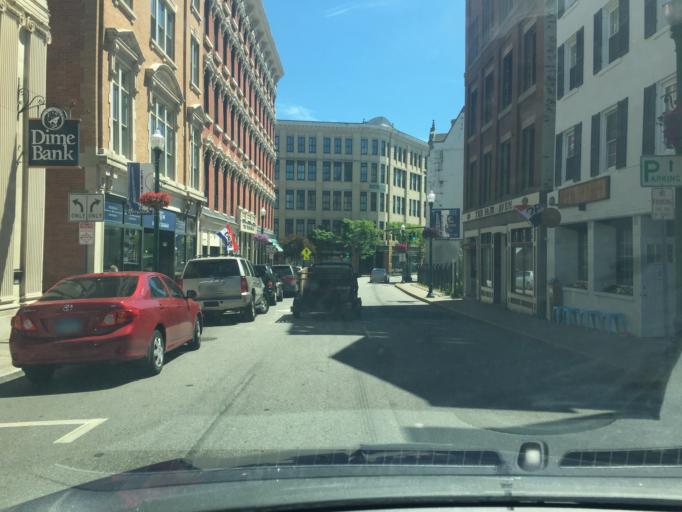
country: US
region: Connecticut
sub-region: New London County
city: Norwich
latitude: 41.5250
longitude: -72.0758
